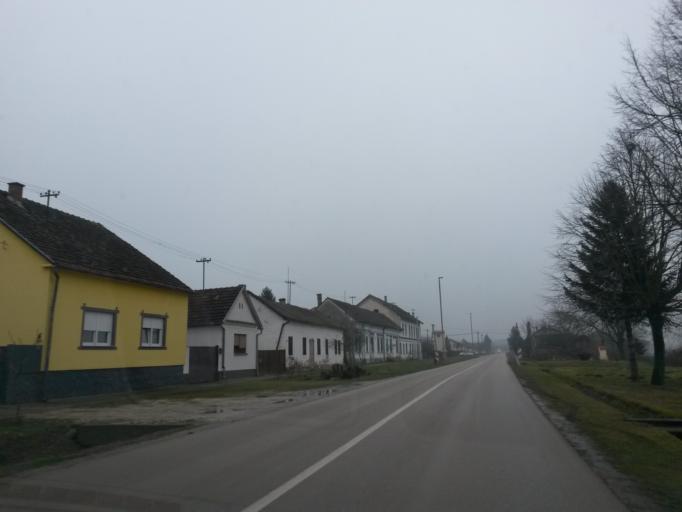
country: HR
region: Vukovarsko-Srijemska
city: Cerna
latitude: 45.1959
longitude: 18.6905
